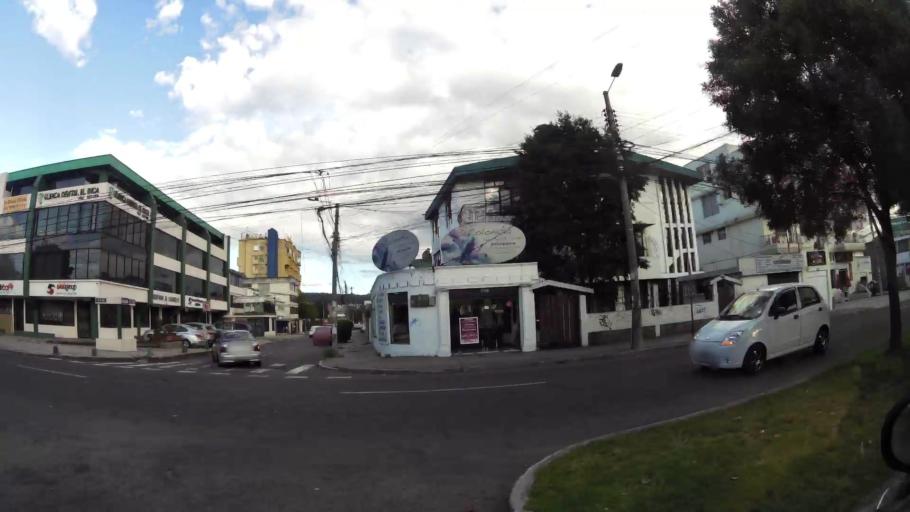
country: EC
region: Pichincha
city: Quito
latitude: -0.1583
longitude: -78.4826
